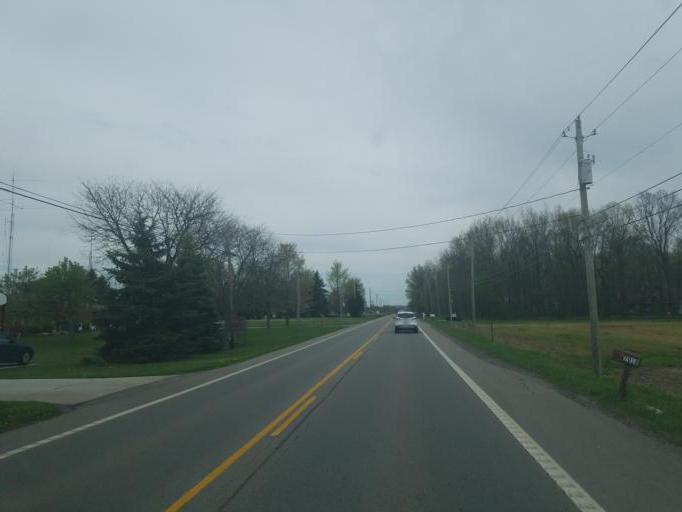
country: US
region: Ohio
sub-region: Wayne County
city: Orrville
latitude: 40.8853
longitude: -81.7633
